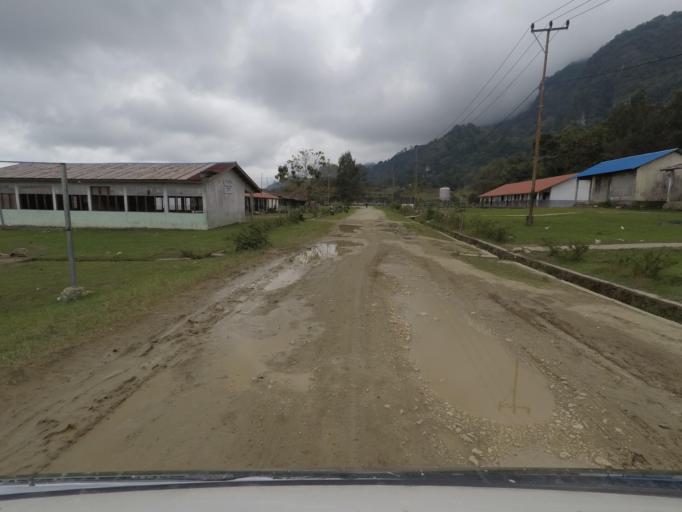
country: TL
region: Baucau
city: Venilale
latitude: -8.7355
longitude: 126.3704
